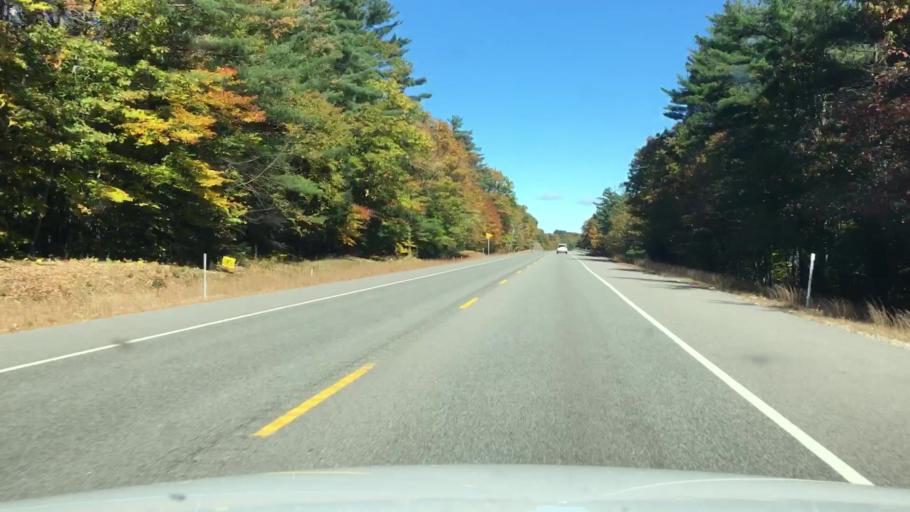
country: US
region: New Hampshire
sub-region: Carroll County
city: Sanbornville
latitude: 43.5107
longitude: -71.0288
